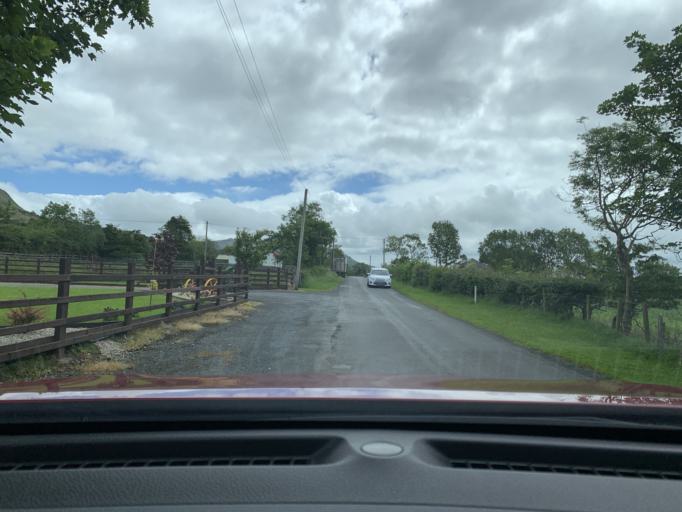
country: IE
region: Connaught
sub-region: Sligo
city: Sligo
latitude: 54.3396
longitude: -8.4795
